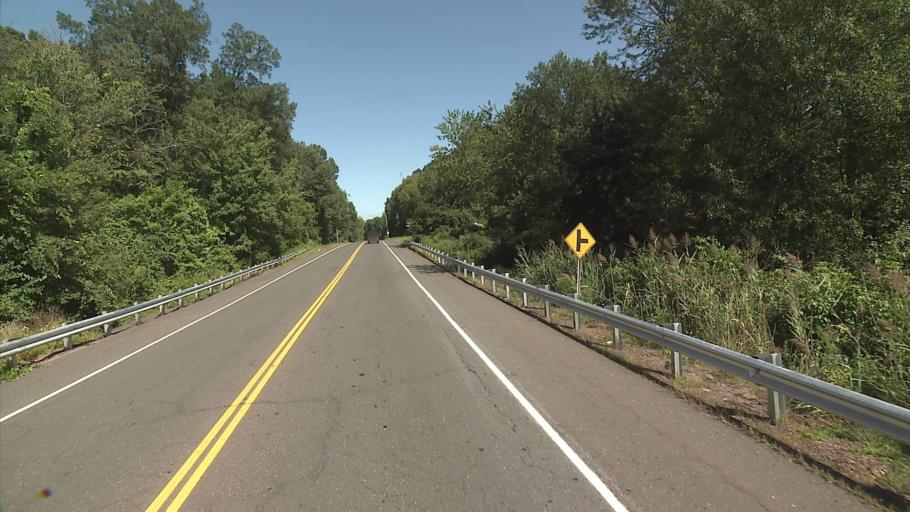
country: US
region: Connecticut
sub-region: Hartford County
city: Weatogue
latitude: 41.8285
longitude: -72.7668
